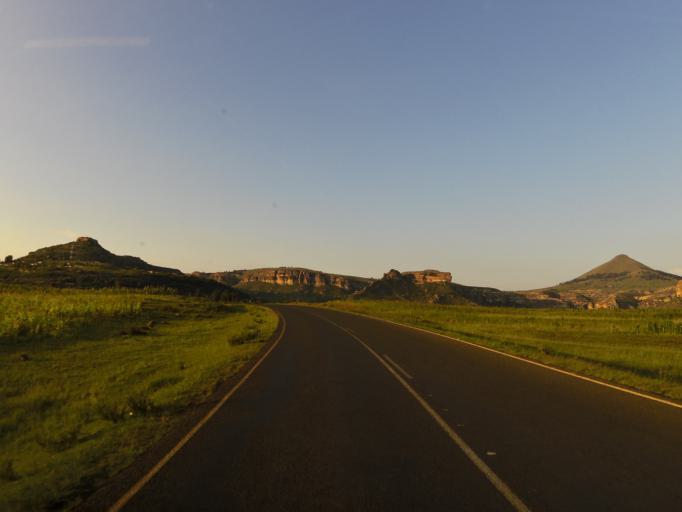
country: LS
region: Leribe
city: Leribe
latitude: -28.8992
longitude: 28.1156
